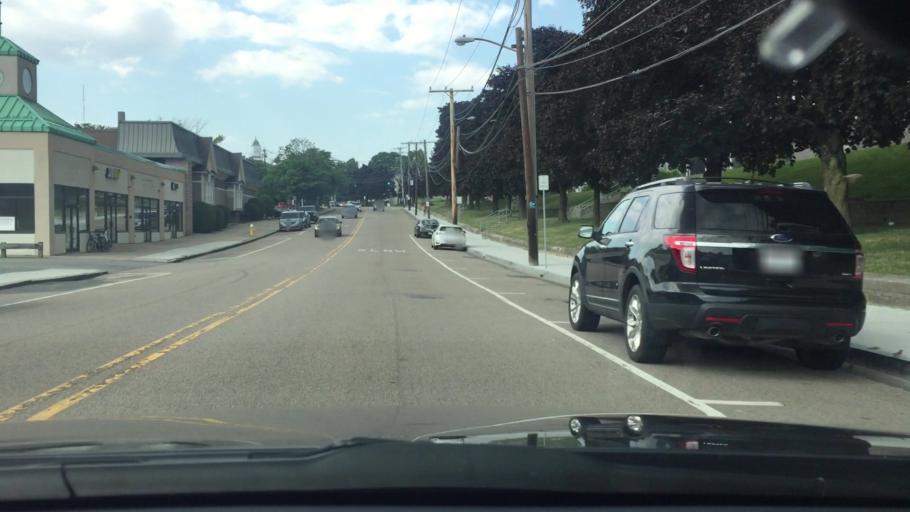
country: US
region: Massachusetts
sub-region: Norfolk County
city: Needham
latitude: 42.2855
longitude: -71.2356
